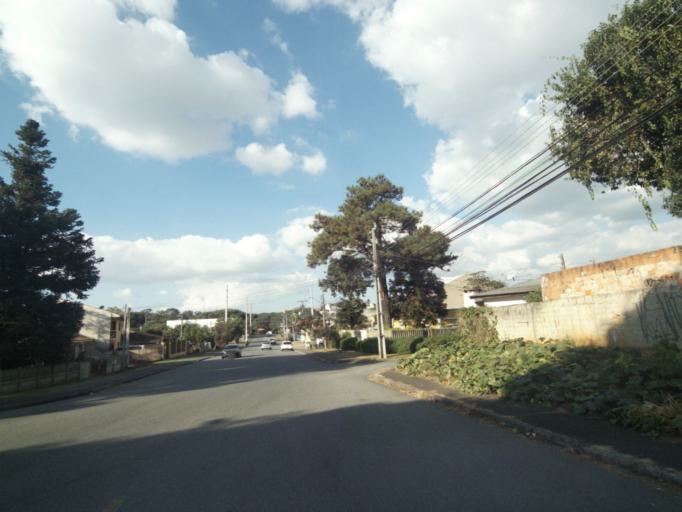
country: BR
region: Parana
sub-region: Curitiba
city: Curitiba
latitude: -25.4574
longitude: -49.2530
